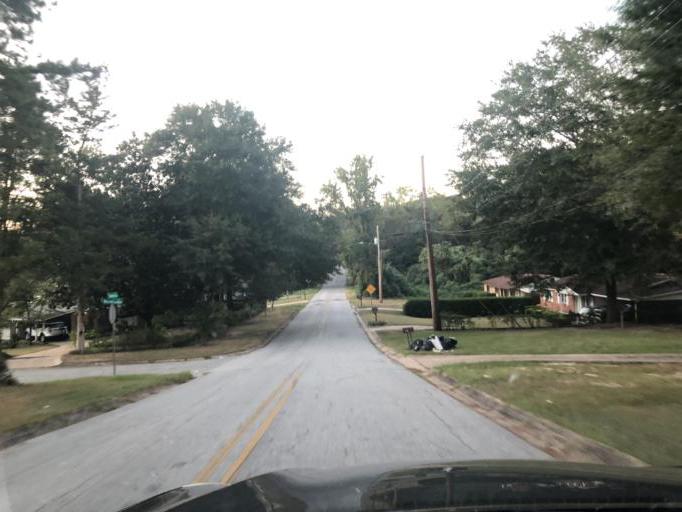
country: US
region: Georgia
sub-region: Muscogee County
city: Columbus
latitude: 32.4708
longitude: -84.8994
